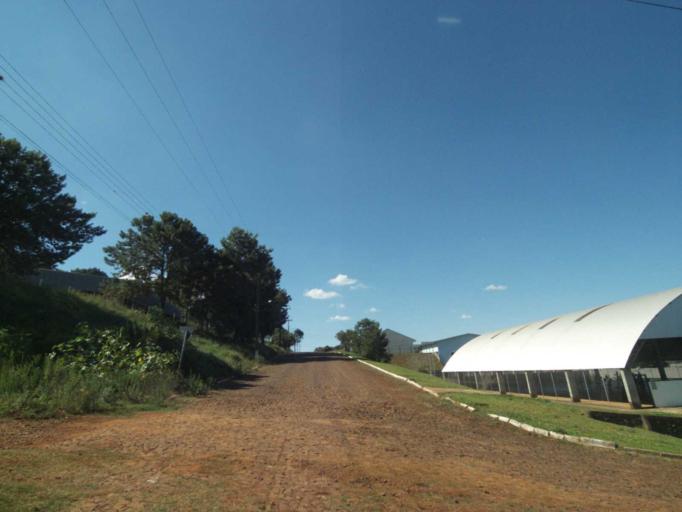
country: BR
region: Parana
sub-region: Laranjeiras Do Sul
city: Laranjeiras do Sul
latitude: -25.3852
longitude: -52.2054
